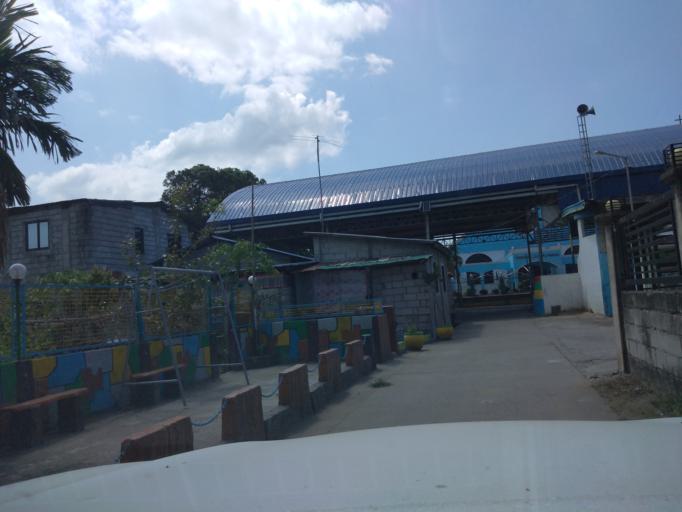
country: PH
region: Central Luzon
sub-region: Province of Pampanga
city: Lourdes
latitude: 15.0195
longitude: 120.8495
